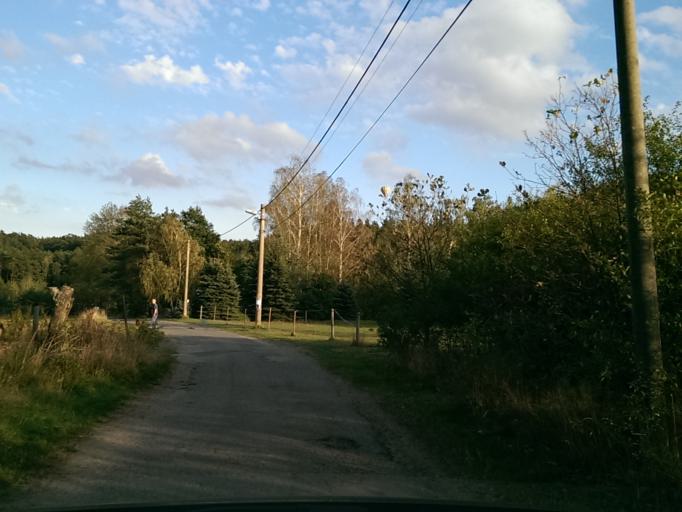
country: CZ
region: Central Bohemia
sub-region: Okres Mlada Boleslav
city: Zd'ar
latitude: 50.5303
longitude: 15.1124
